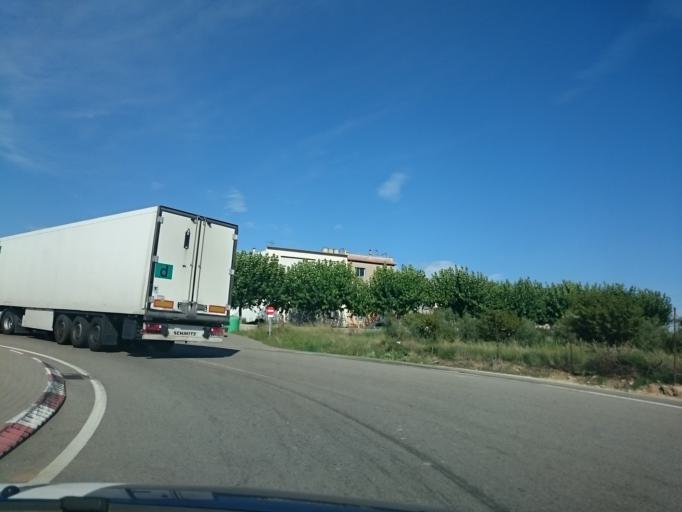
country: ES
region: Catalonia
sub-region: Provincia de Barcelona
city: Castellet
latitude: 41.2624
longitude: 1.6003
